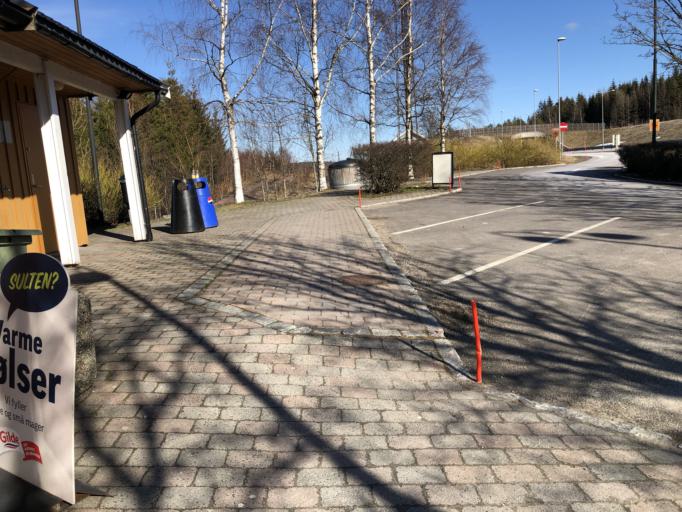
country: NO
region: Vestfold
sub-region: Stokke
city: Stokke
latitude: 59.2506
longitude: 10.2870
